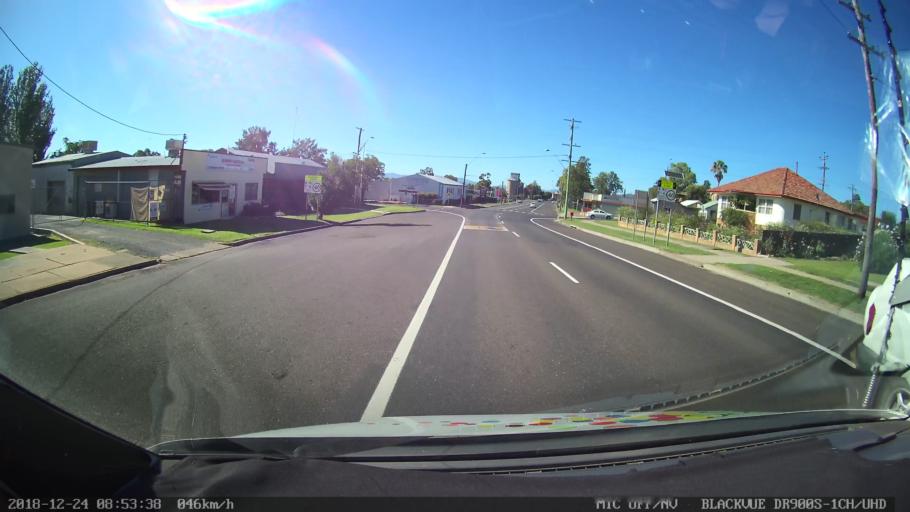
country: AU
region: New South Wales
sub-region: Liverpool Plains
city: Quirindi
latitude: -31.4999
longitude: 150.6812
